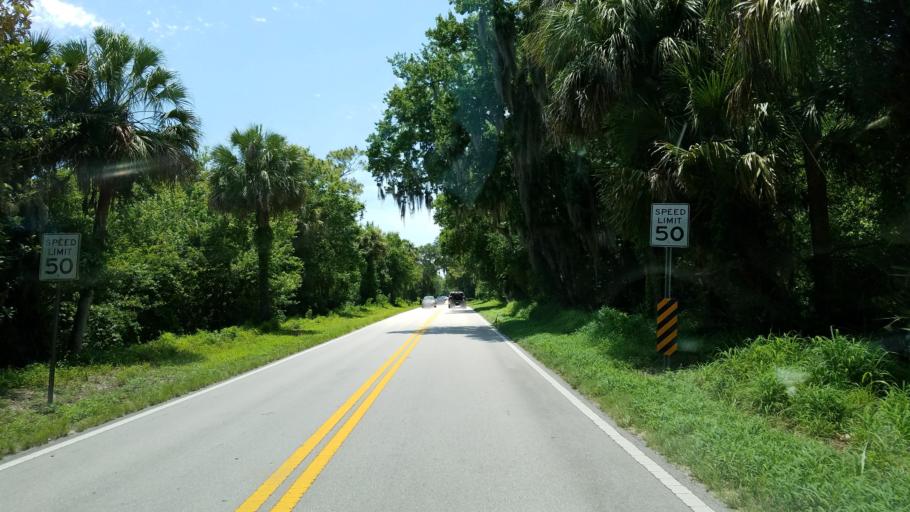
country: US
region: Florida
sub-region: Martin County
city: Indiantown
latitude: 27.1622
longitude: -80.5736
